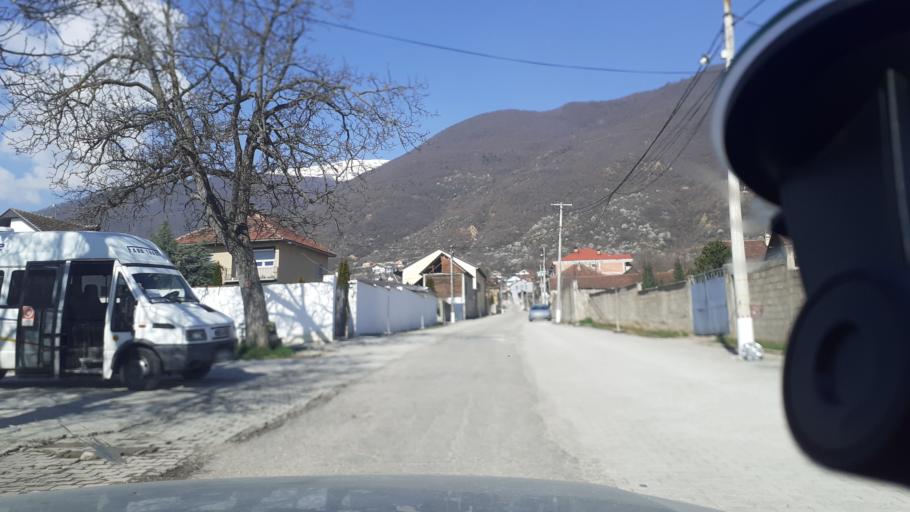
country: MK
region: Tearce
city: Slatino
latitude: 42.0696
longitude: 21.0460
